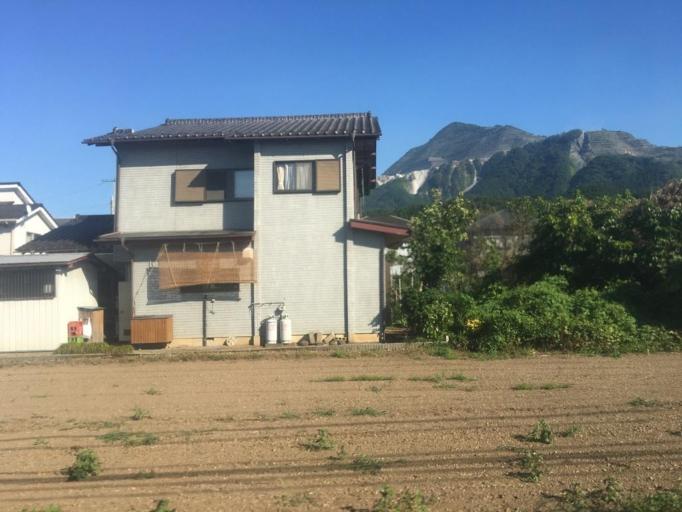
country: JP
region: Saitama
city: Chichibu
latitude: 35.9785
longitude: 139.0764
